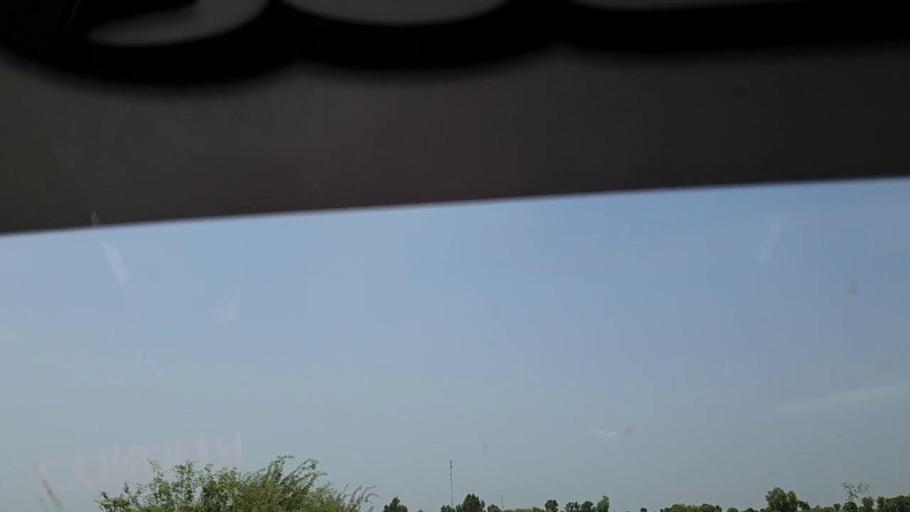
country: PK
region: Sindh
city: Adilpur
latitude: 27.9148
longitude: 69.2092
